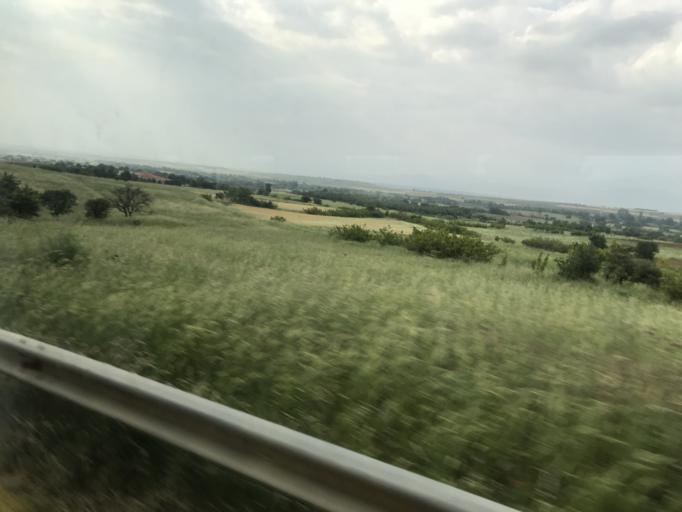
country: GR
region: East Macedonia and Thrace
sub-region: Nomos Rodopis
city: Sapes
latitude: 41.0304
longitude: 25.6834
